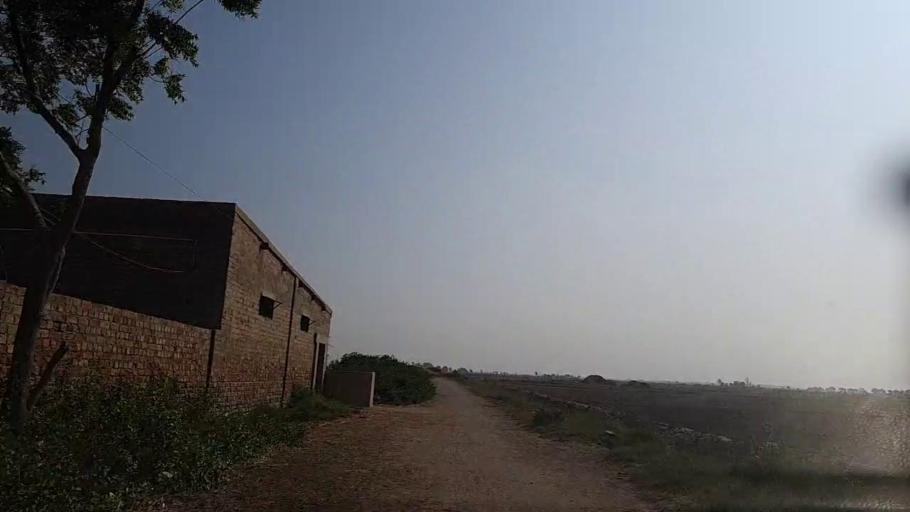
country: PK
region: Sindh
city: Mirpur Batoro
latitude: 24.5790
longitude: 68.2250
